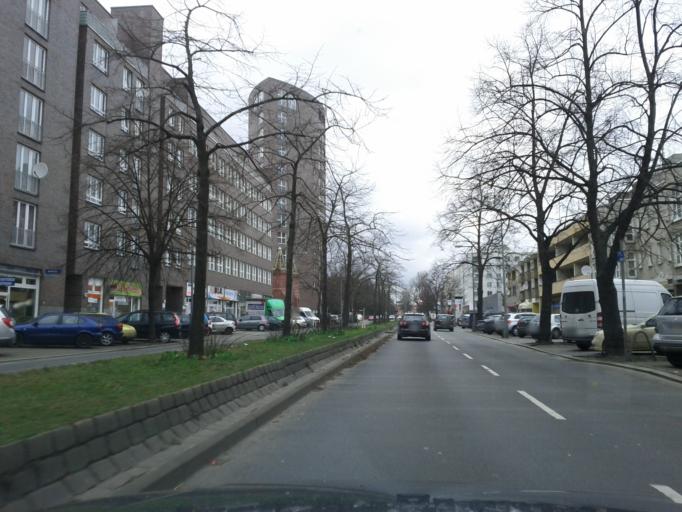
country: DE
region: Berlin
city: Gesundbrunnen
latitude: 52.5433
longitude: 13.3922
